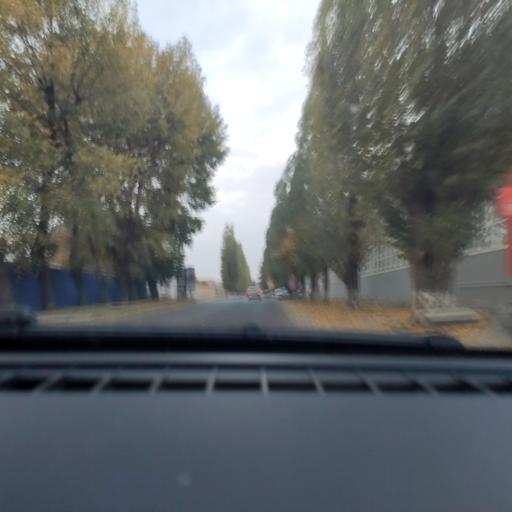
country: RU
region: Voronezj
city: Voronezh
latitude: 51.6519
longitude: 39.2810
